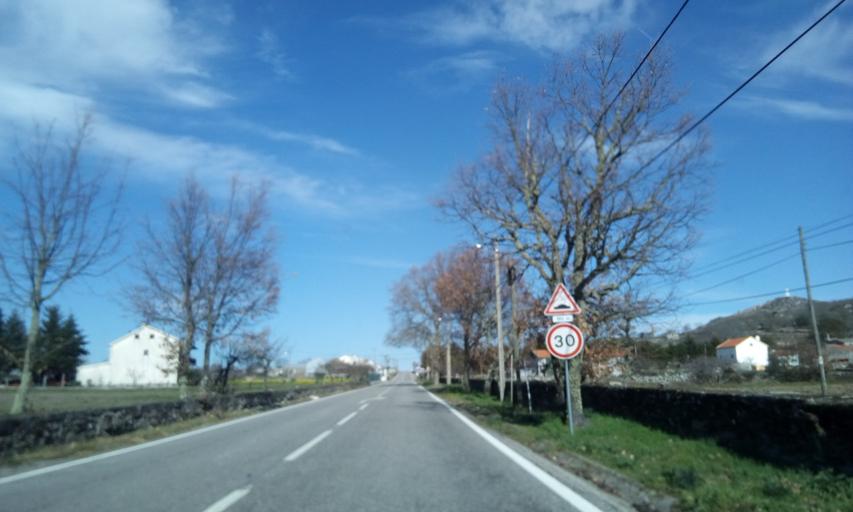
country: PT
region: Guarda
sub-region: Guarda
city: Sequeira
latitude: 40.5901
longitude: -7.1426
